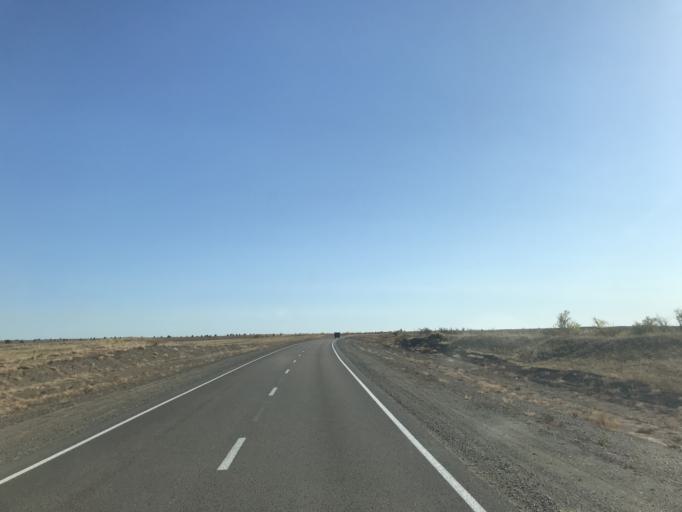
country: KZ
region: Pavlodar
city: Koktobe
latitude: 51.8579
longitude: 77.4497
